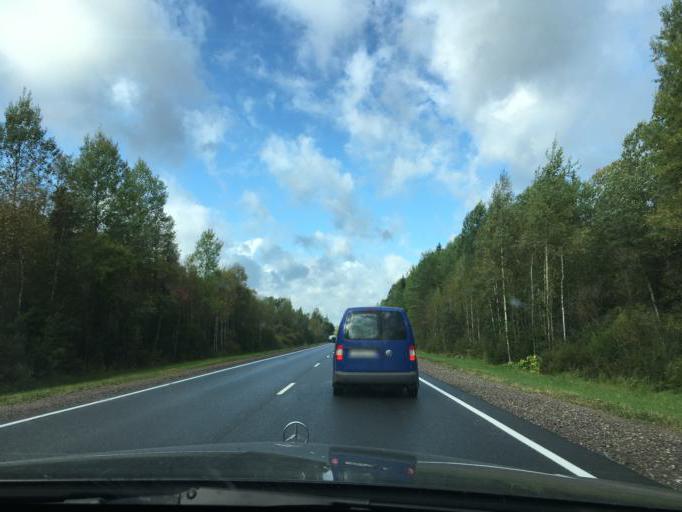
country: RU
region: Tverskaya
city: Nelidovo
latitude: 56.2769
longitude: 32.7184
